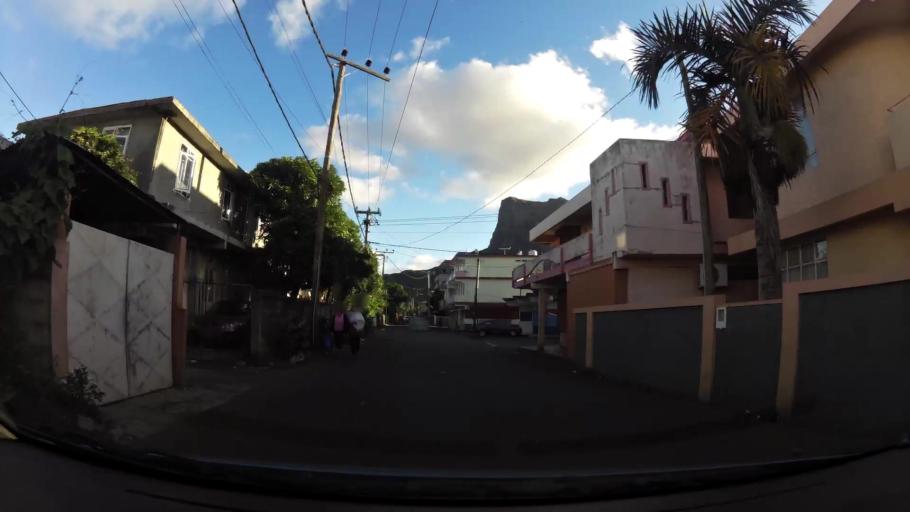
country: MU
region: Plaines Wilhems
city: Quatre Bornes
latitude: -20.2581
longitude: 57.4674
